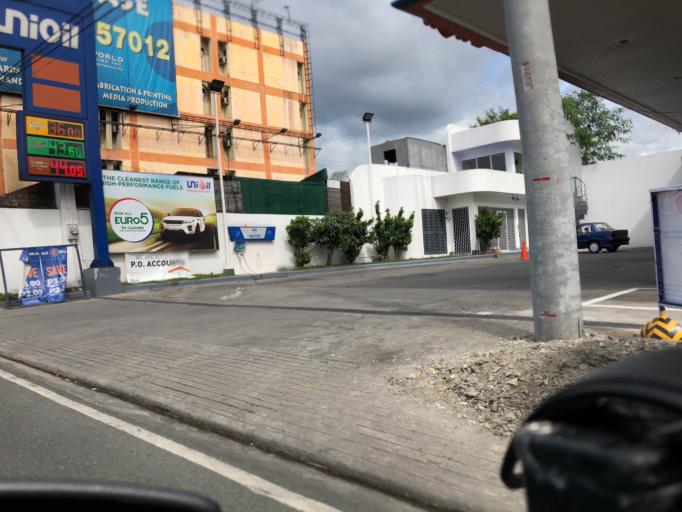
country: PH
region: Calabarzon
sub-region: Province of Rizal
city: San Mateo
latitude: 14.7244
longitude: 121.0612
